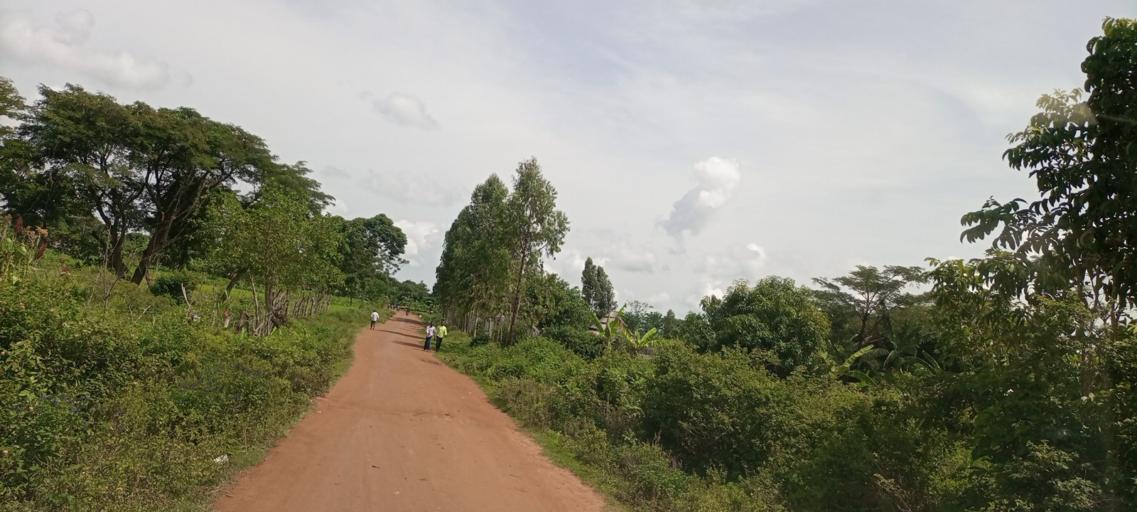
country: UG
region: Eastern Region
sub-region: Budaka District
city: Budaka
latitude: 1.1730
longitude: 33.9316
